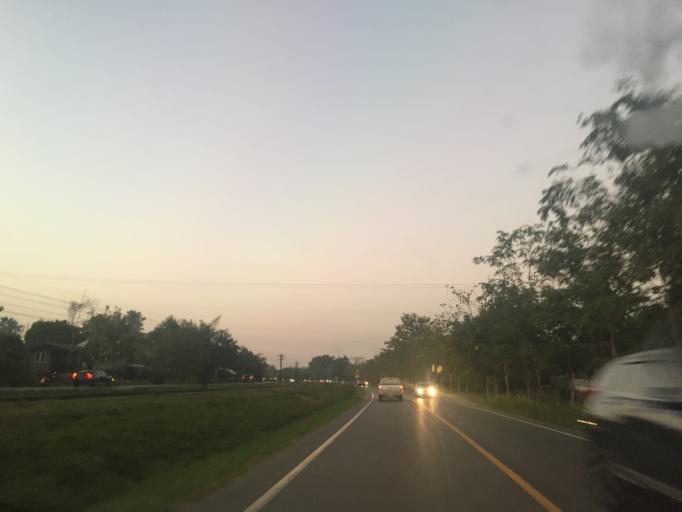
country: TH
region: Chiang Mai
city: Saraphi
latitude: 18.6985
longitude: 99.0459
